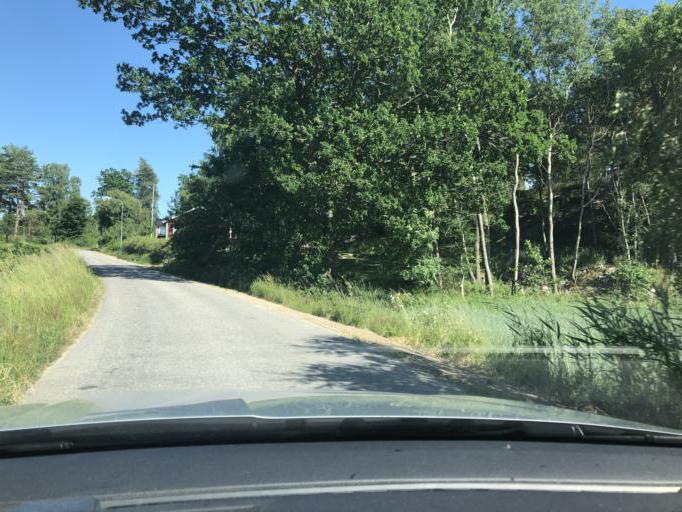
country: SE
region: Blekinge
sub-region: Karlshamns Kommun
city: Morrum
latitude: 56.1714
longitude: 14.7291
